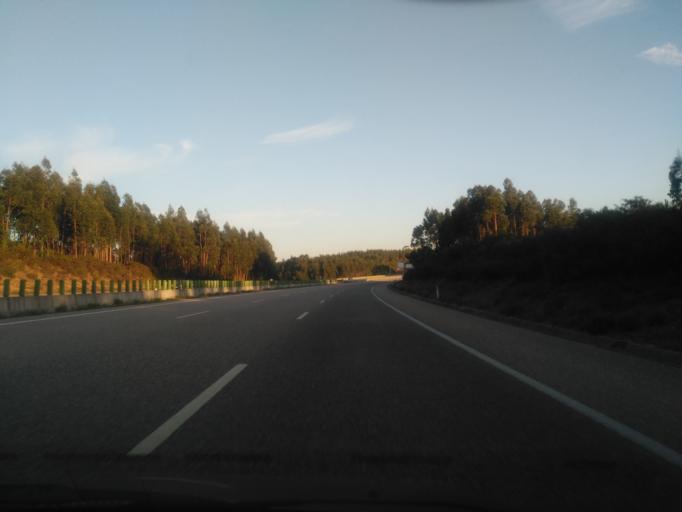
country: PT
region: Leiria
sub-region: Pombal
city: Lourical
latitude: 39.9828
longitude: -8.7868
